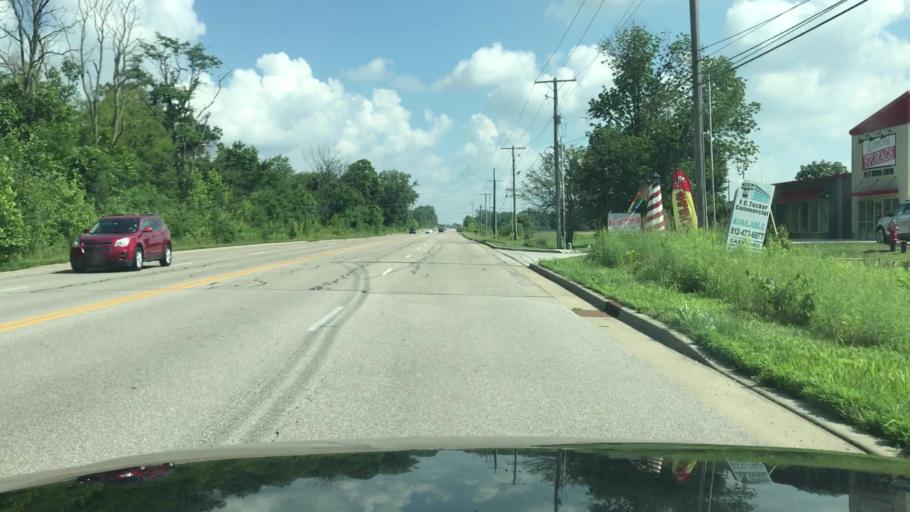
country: US
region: Indiana
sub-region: Vanderburgh County
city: Melody Hill
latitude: 38.0175
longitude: -87.4922
